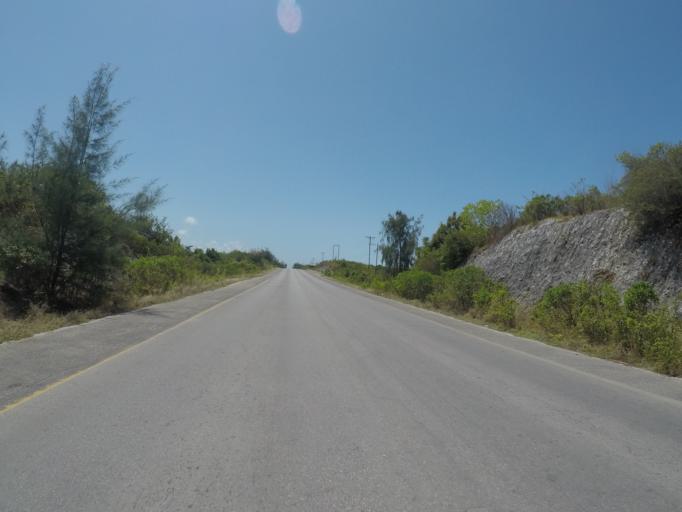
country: TZ
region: Zanzibar Central/South
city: Nganane
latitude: -6.2918
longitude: 39.5372
